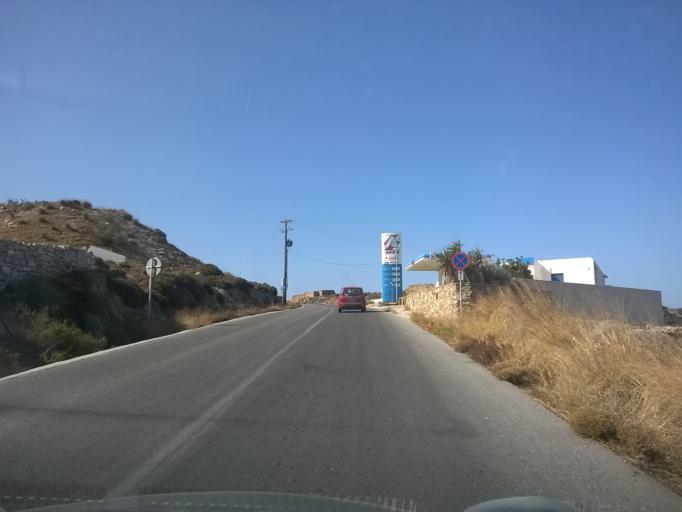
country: GR
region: South Aegean
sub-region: Nomos Kykladon
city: Filotion
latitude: 37.0911
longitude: 25.4486
